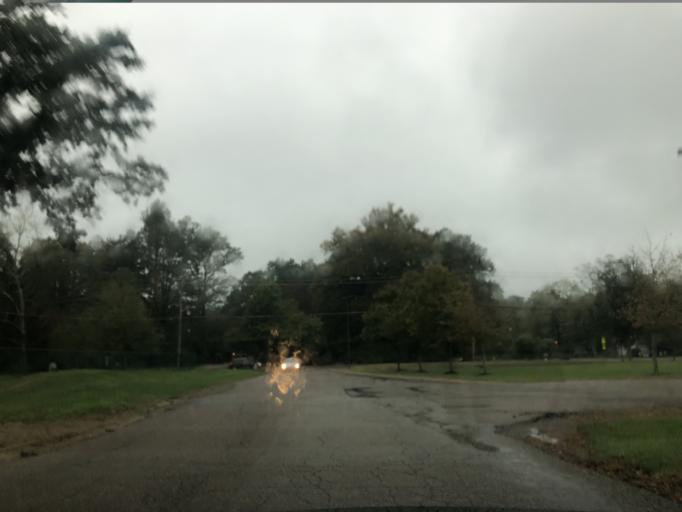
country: US
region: Ohio
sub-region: Hamilton County
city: The Village of Indian Hill
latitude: 39.2621
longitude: -84.2852
